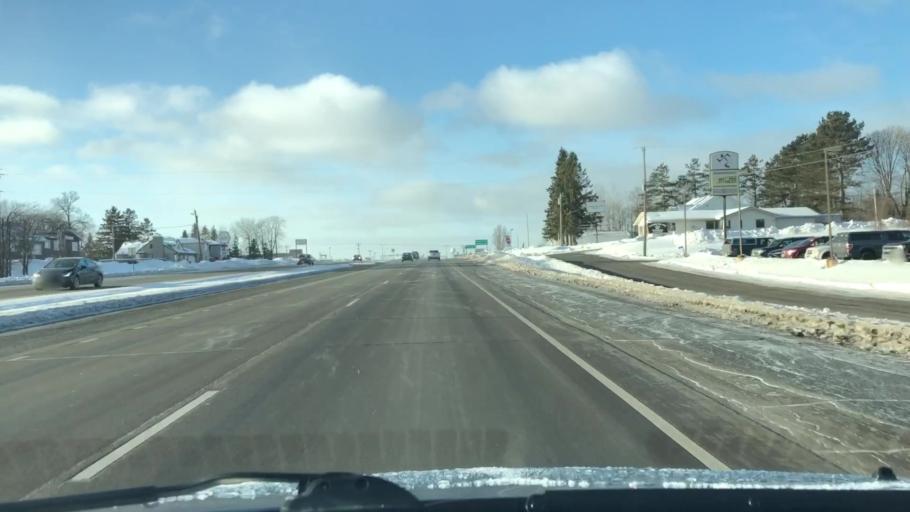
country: US
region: Minnesota
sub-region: Saint Louis County
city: Hermantown
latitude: 46.8246
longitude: -92.1907
